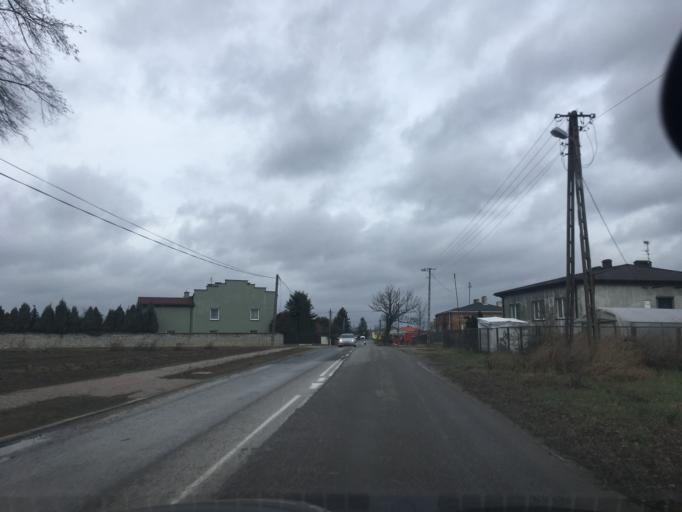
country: PL
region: Masovian Voivodeship
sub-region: Powiat piaseczynski
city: Lesznowola
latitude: 52.1053
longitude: 20.9312
